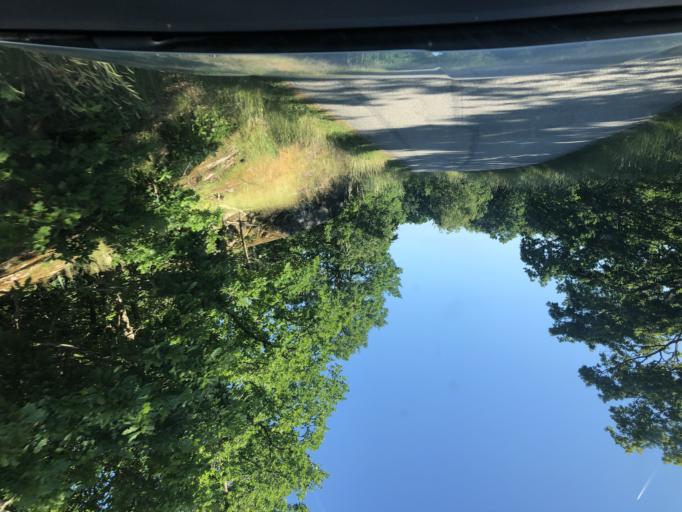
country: SE
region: Blekinge
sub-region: Karlshamns Kommun
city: Morrum
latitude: 56.1612
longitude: 14.8013
